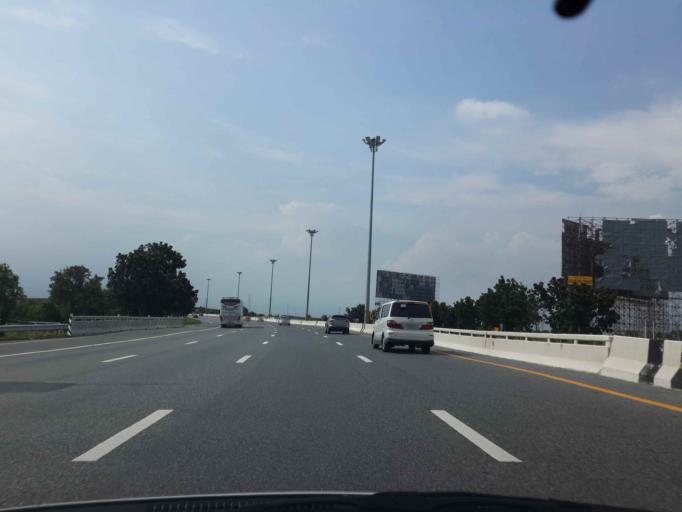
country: TH
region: Chon Buri
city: Phan Thong
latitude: 13.4928
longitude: 101.0466
